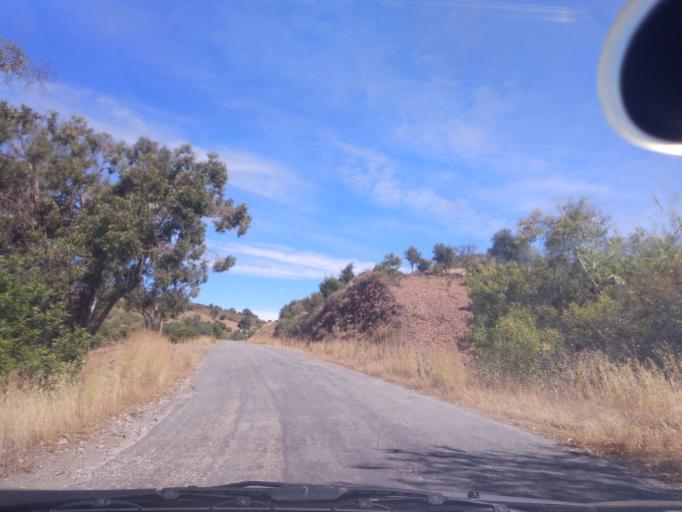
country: PT
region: Faro
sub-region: Olhao
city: Moncarapacho
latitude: 37.1674
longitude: -7.8024
